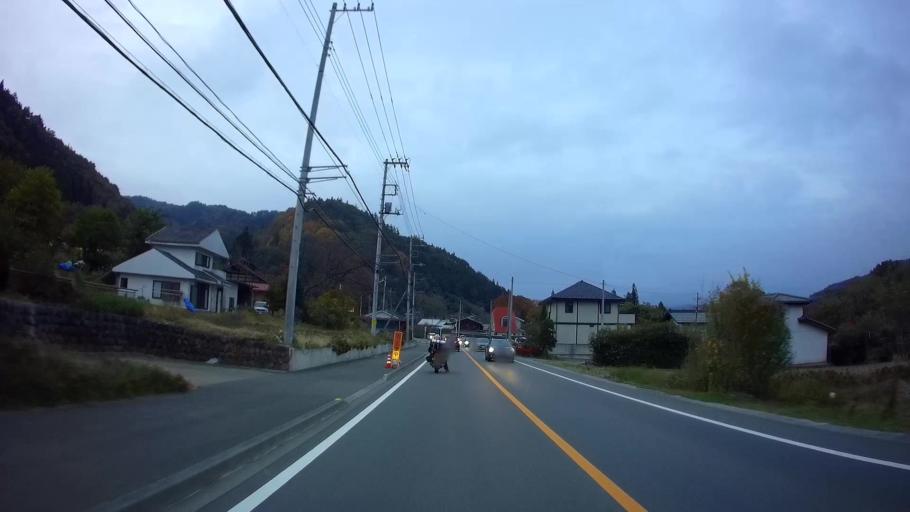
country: JP
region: Gunma
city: Nakanojomachi
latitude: 36.5602
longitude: 138.7657
